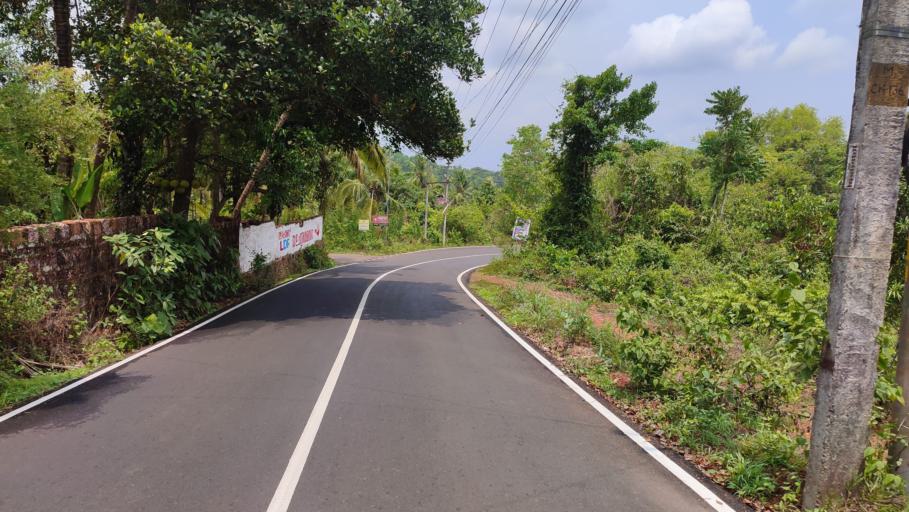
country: IN
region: Kerala
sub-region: Kasaragod District
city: Kannangad
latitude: 12.3205
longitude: 75.1368
